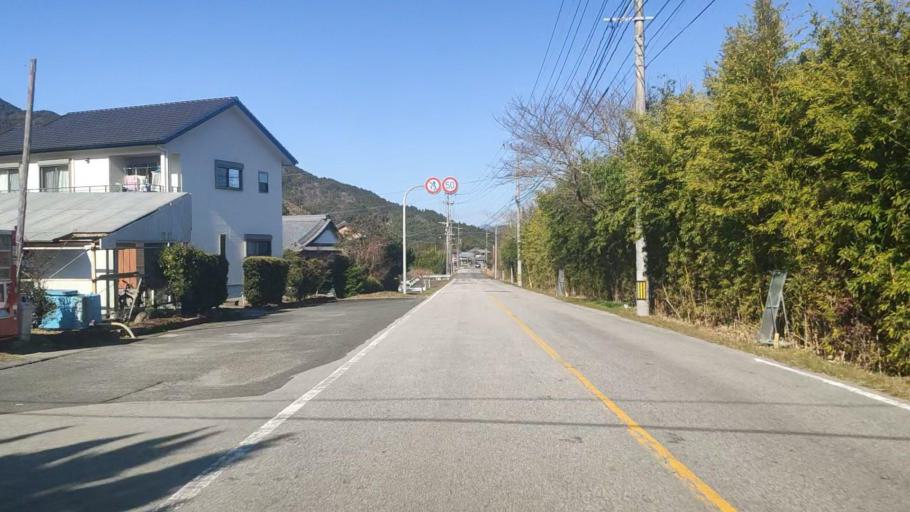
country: JP
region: Oita
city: Saiki
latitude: 32.9117
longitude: 131.9295
